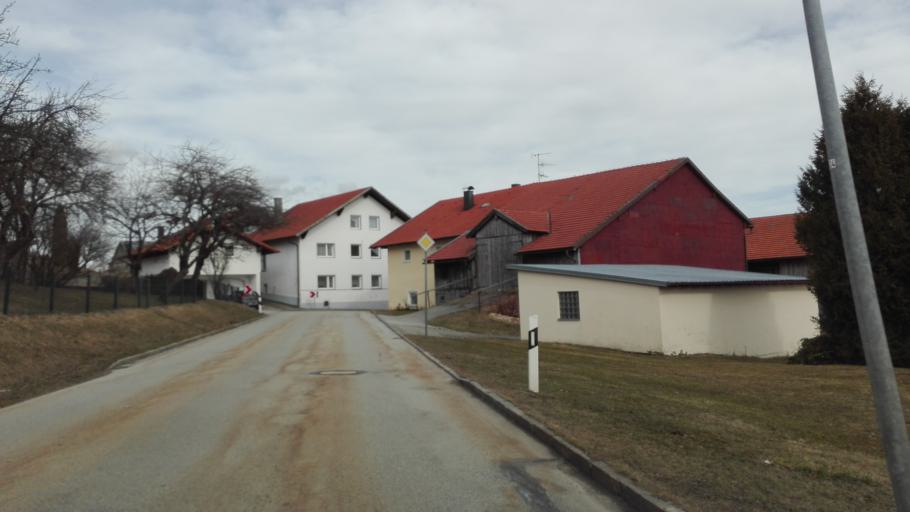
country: DE
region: Bavaria
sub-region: Lower Bavaria
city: Wegscheid
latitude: 48.6231
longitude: 13.7739
